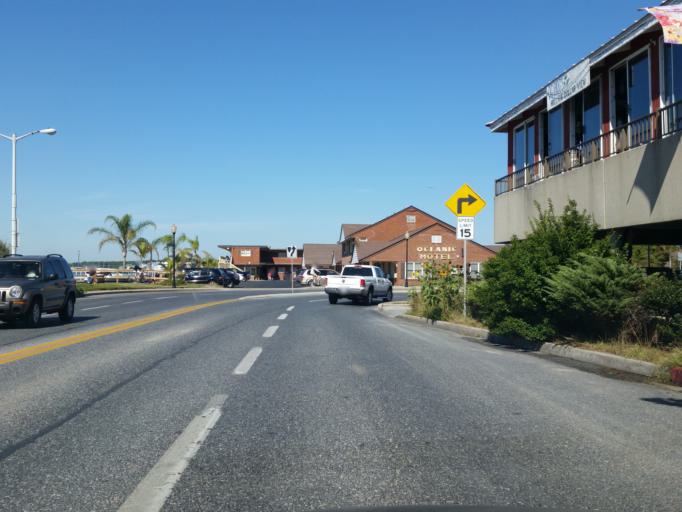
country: US
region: Maryland
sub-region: Worcester County
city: Ocean City
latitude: 38.3255
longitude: -75.0887
